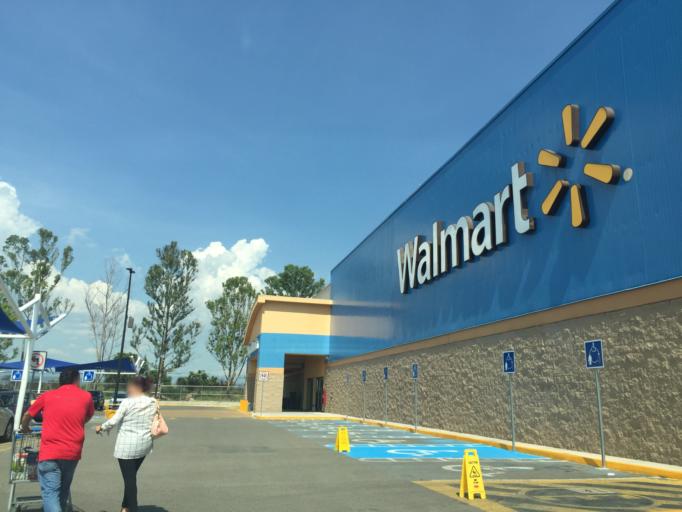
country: MX
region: Guanajuato
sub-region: Leon
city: La Ermita
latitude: 21.1729
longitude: -101.7328
